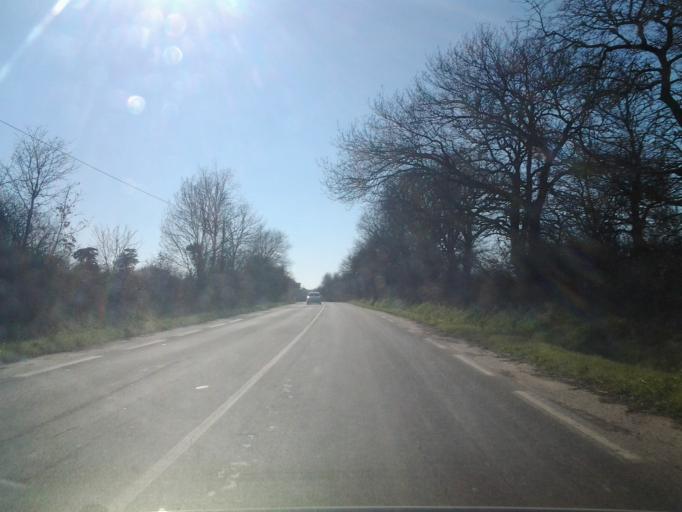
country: FR
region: Pays de la Loire
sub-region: Departement de la Vendee
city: Saint-Mathurin
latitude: 46.5475
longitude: -1.7330
